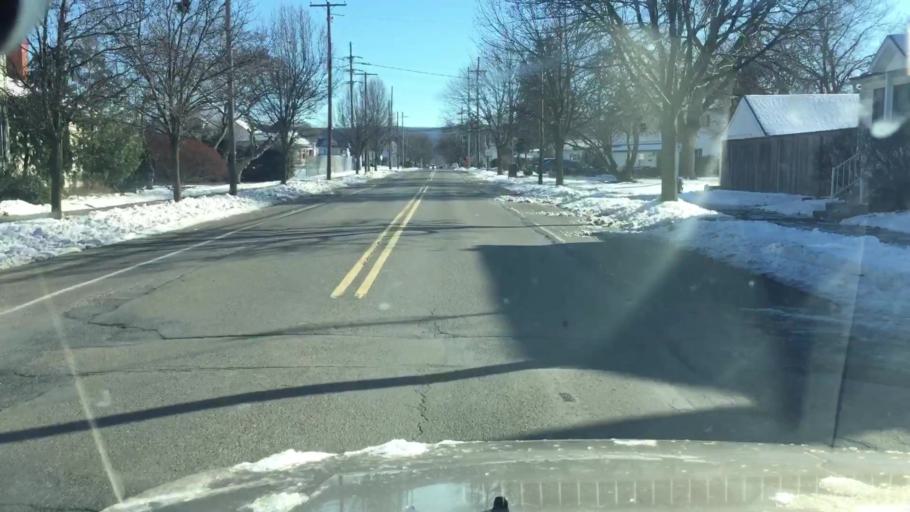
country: US
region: Pennsylvania
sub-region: Luzerne County
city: East Berwick
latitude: 41.0632
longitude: -76.2280
